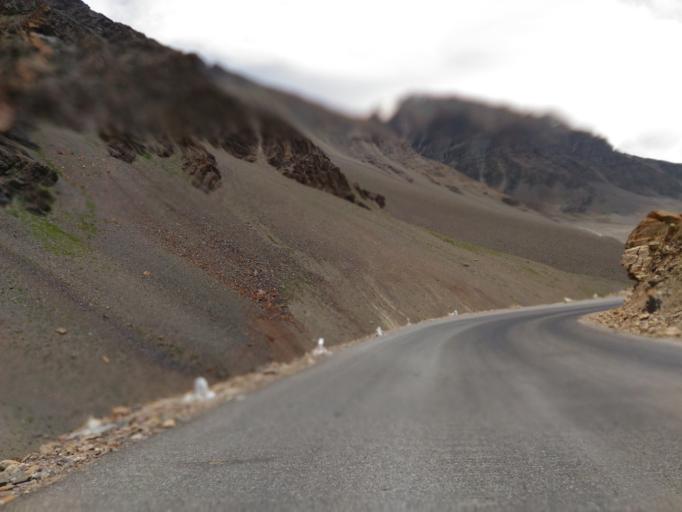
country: IN
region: Himachal Pradesh
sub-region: Lahul and Spiti
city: Kyelang
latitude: 32.7911
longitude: 77.3347
